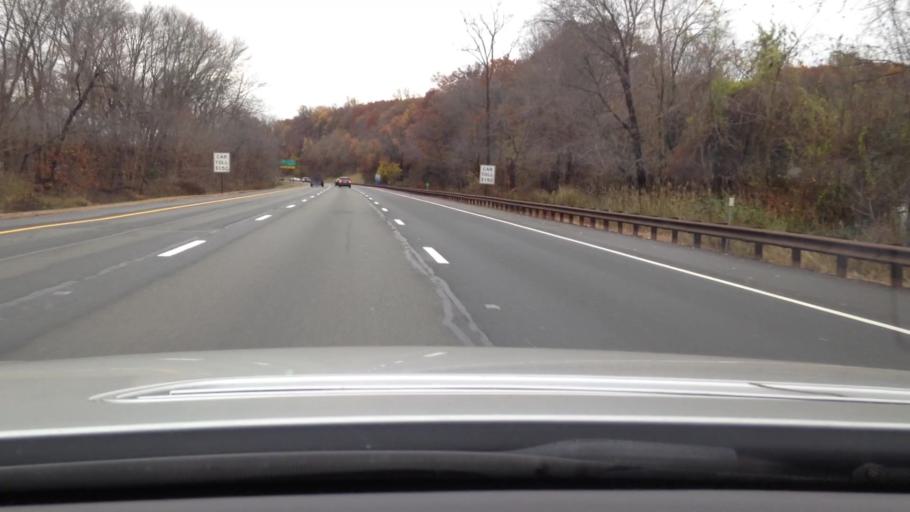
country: US
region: New Jersey
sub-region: Bergen County
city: Ho-Ho-Kus
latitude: 40.9947
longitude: -74.0729
